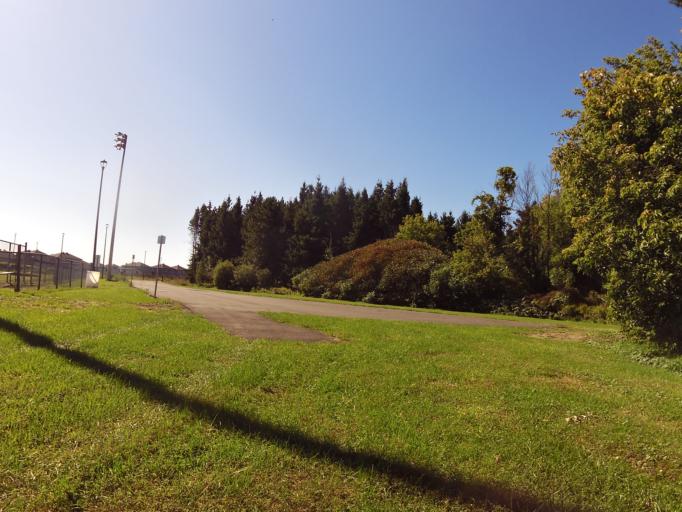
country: CA
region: Ontario
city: Casselman
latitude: 45.2689
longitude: -75.2845
